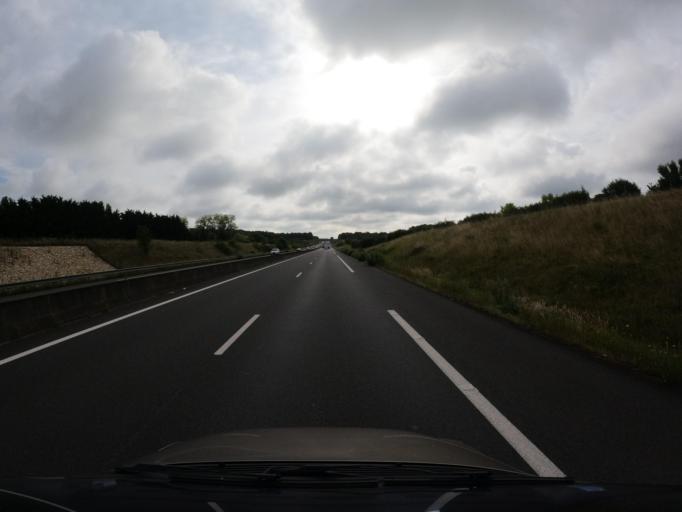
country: FR
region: Centre
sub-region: Departement d'Indre-et-Loire
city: Monts
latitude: 47.3066
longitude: 0.6431
